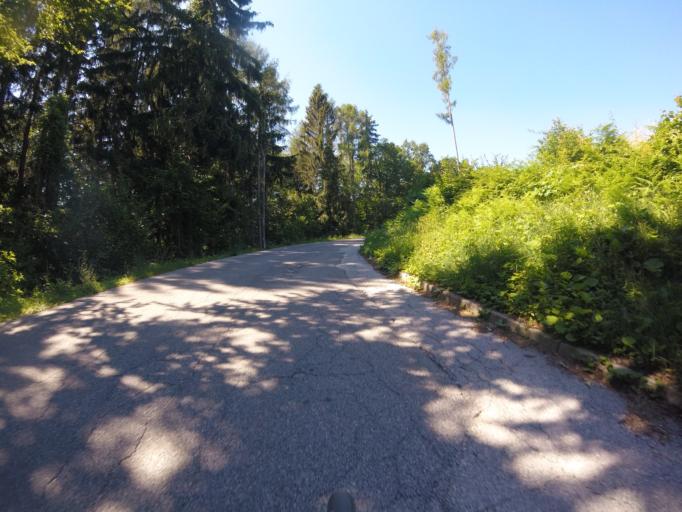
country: SI
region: Kostanjevica na Krki
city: Kostanjevica na Krki
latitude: 45.8139
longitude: 15.5153
